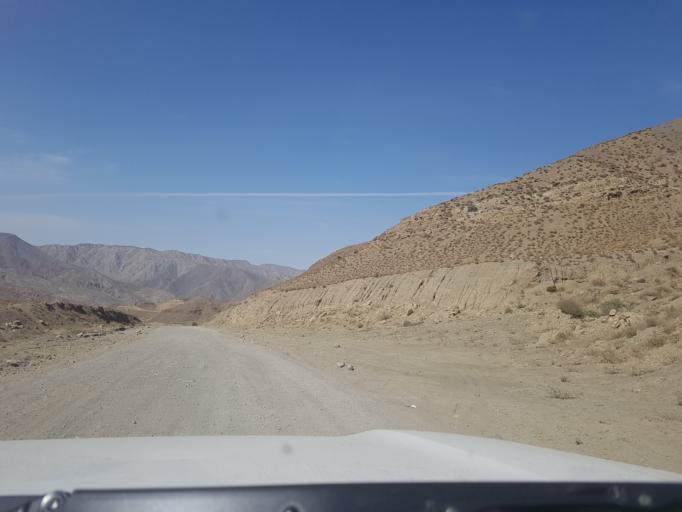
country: TM
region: Ahal
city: Baharly
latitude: 38.4484
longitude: 57.0479
